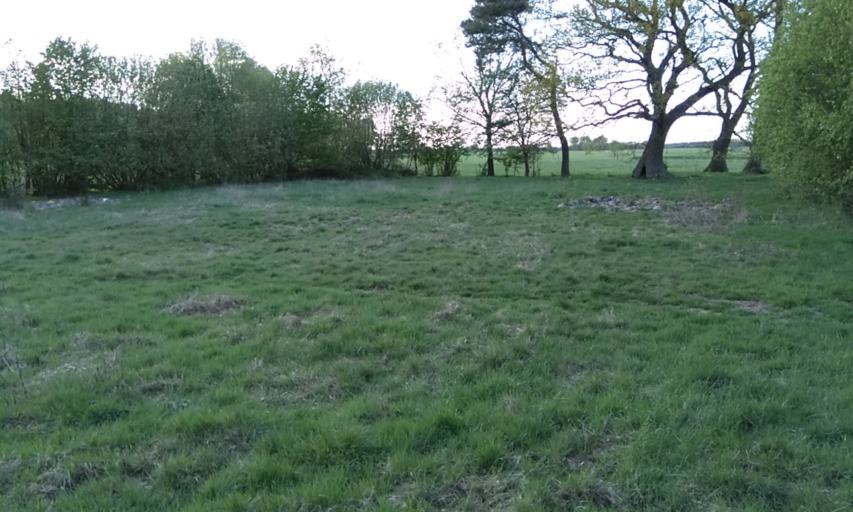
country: DE
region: Lower Saxony
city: Sauensiek
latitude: 53.4069
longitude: 9.5688
